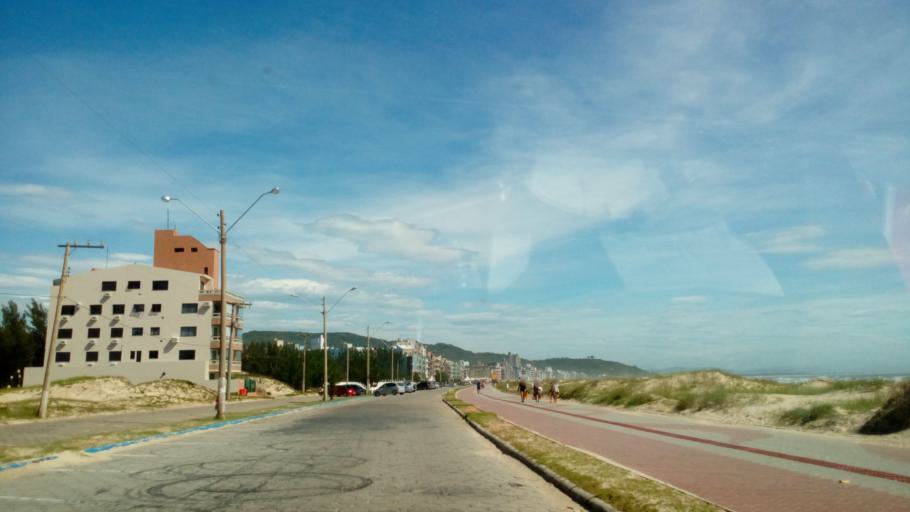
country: BR
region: Santa Catarina
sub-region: Laguna
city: Laguna
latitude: -28.4916
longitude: -48.7638
